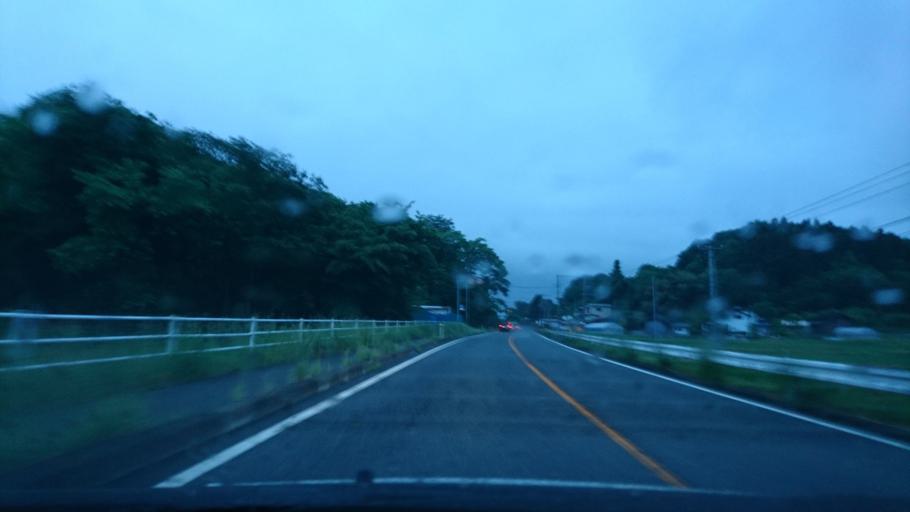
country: JP
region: Iwate
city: Ichinoseki
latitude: 38.7855
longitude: 141.0496
